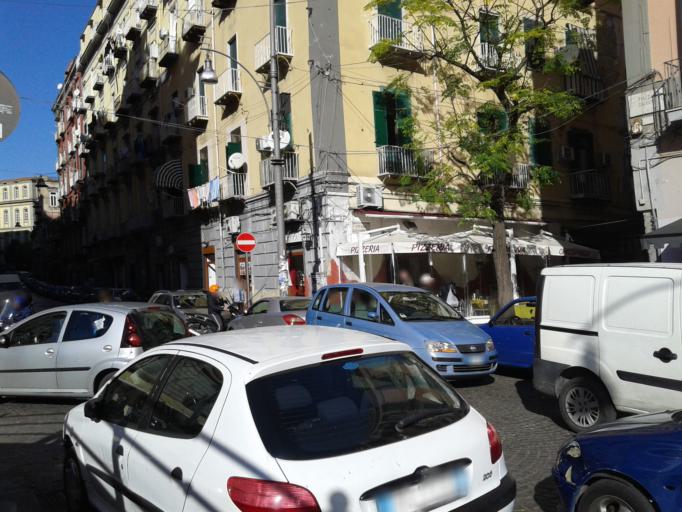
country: IT
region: Campania
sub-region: Provincia di Napoli
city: Napoli
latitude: 40.8557
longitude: 14.2549
